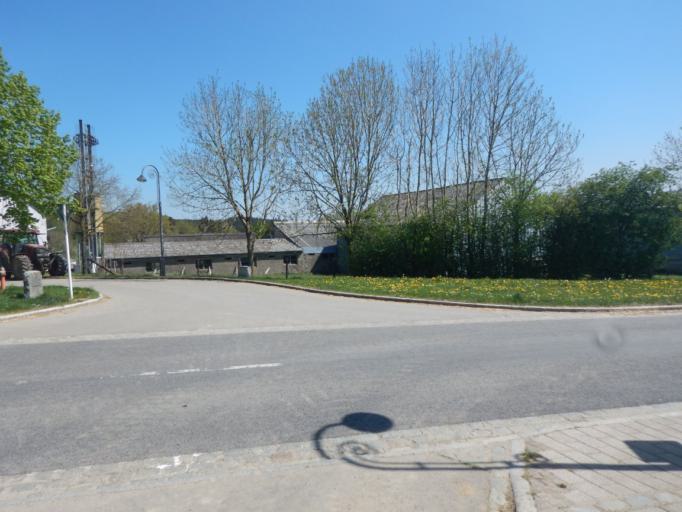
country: LU
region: Diekirch
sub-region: Canton de Clervaux
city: Troisvierges
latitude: 50.1476
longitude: 6.0118
